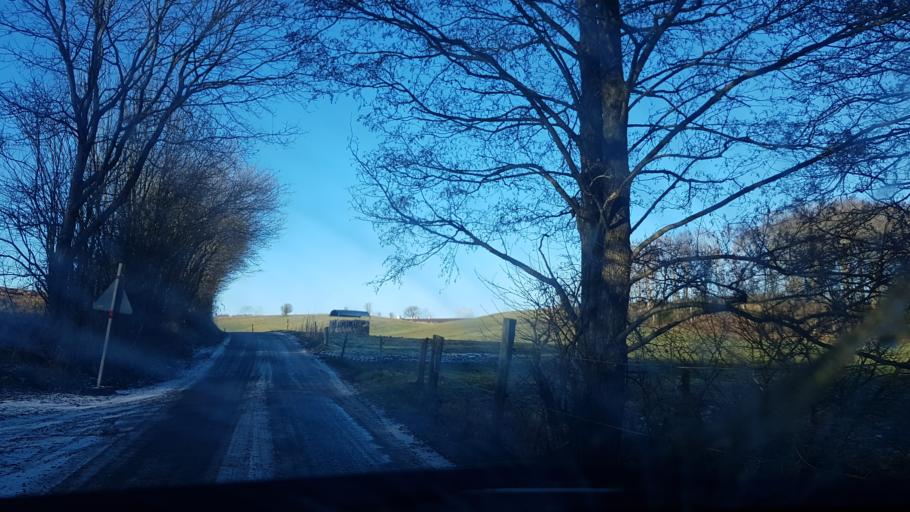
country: DK
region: South Denmark
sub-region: Fredericia Kommune
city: Taulov
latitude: 55.5262
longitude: 9.6521
